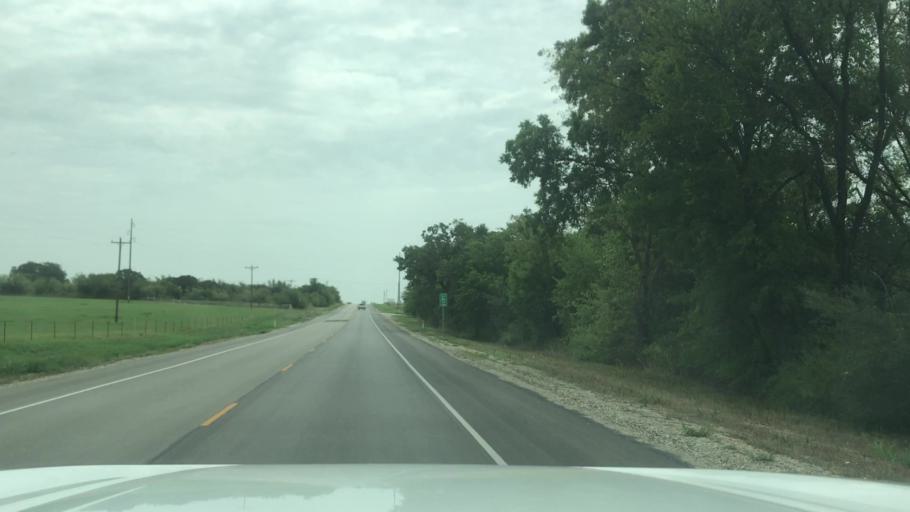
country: US
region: Texas
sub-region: Erath County
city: Dublin
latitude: 32.0887
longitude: -98.2599
